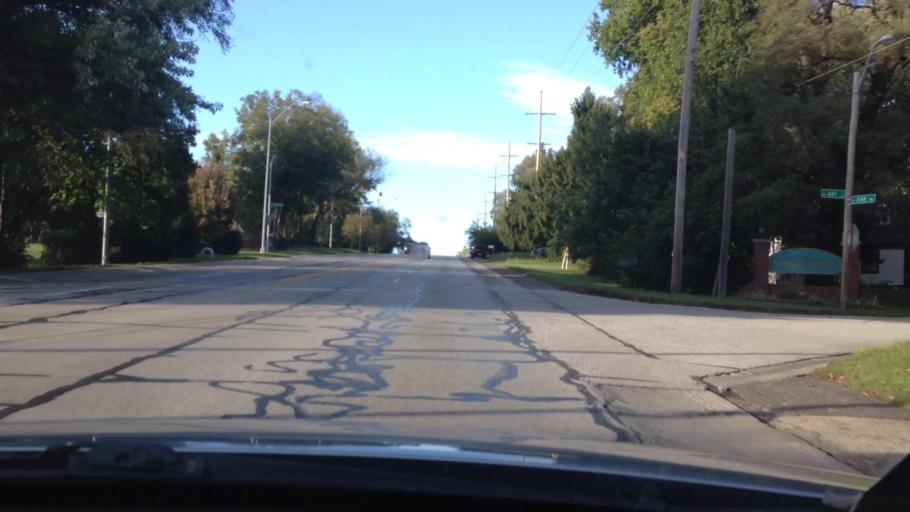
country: US
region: Missouri
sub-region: Platte County
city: Riverside
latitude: 39.1739
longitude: -94.5767
